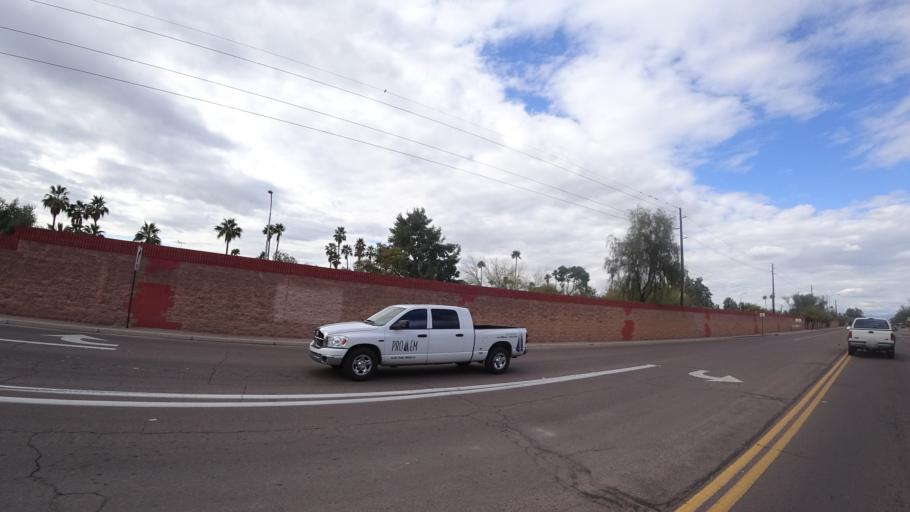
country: US
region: Arizona
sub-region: Maricopa County
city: Scottsdale
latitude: 33.5098
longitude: -111.8916
